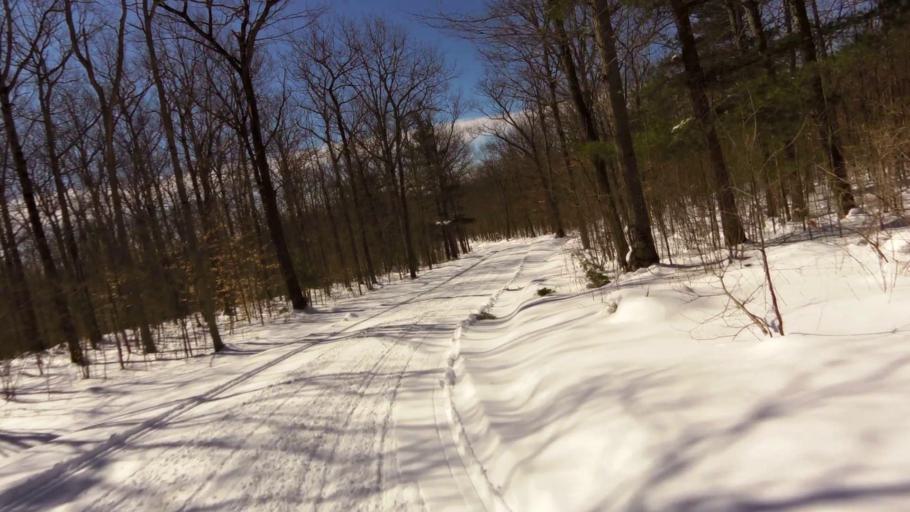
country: US
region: New York
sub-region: Allegany County
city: Houghton
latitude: 42.3382
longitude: -78.2032
